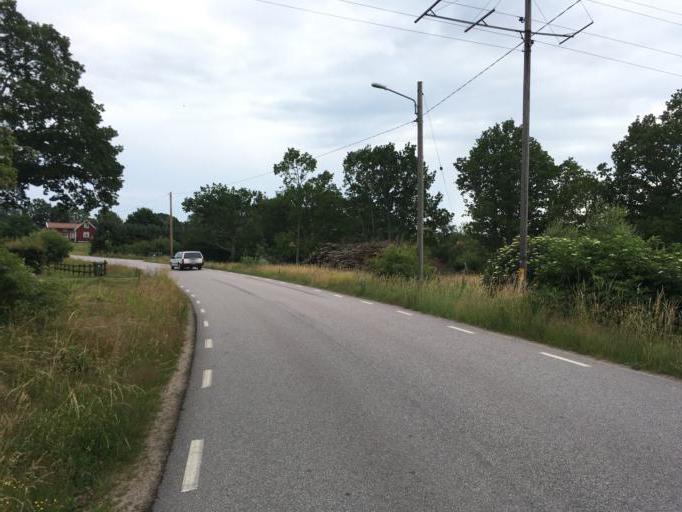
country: SE
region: Blekinge
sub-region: Karlskrona Kommun
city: Sturko
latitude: 56.0935
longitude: 15.6935
